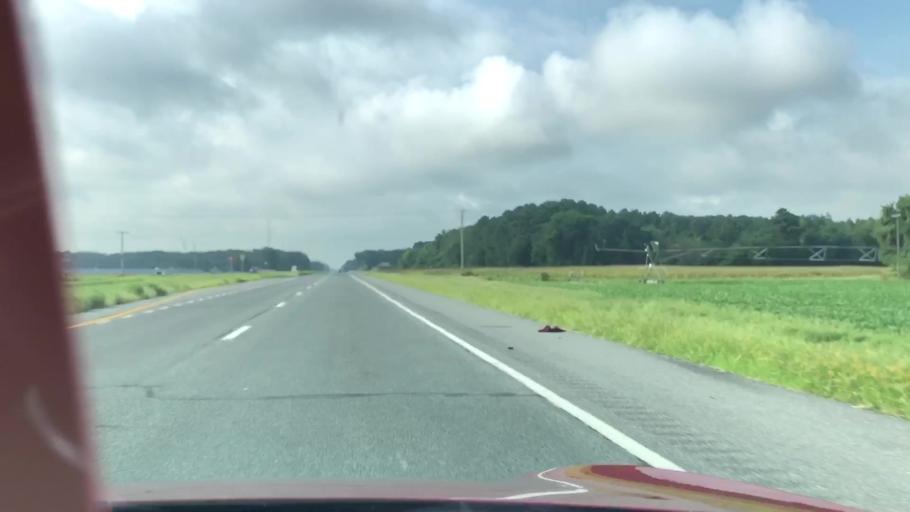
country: US
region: Delaware
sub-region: Sussex County
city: Laurel
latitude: 38.5335
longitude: -75.5568
